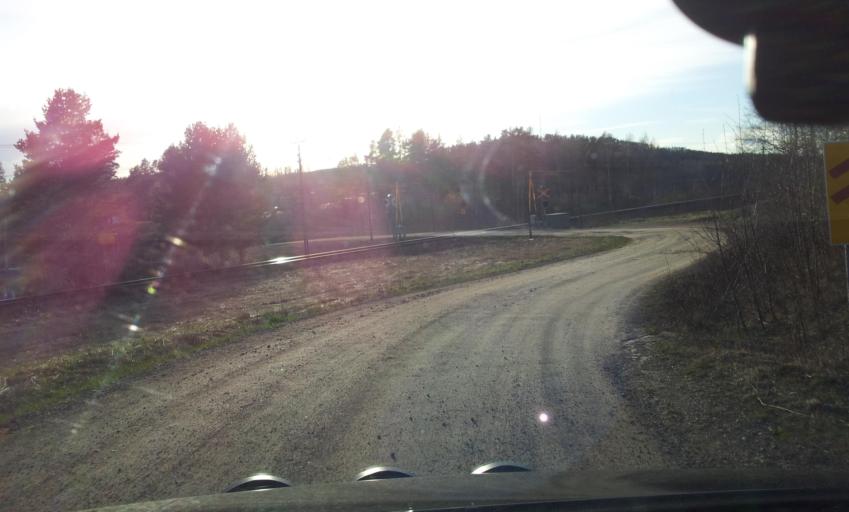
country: SE
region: Vaesternorrland
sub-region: Ange Kommun
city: Ange
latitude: 62.1534
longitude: 15.6784
